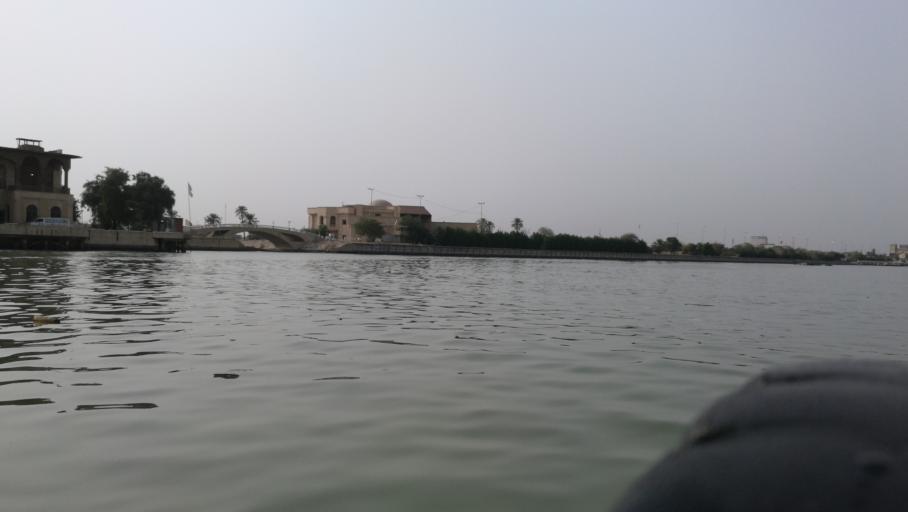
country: IQ
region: Basra Governorate
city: Al Basrah al Qadimah
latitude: 30.4972
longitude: 47.8638
